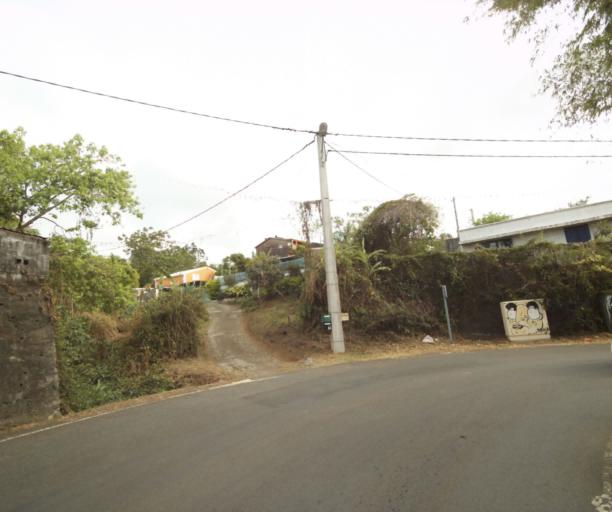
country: RE
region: Reunion
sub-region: Reunion
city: Saint-Paul
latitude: -21.0399
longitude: 55.3057
